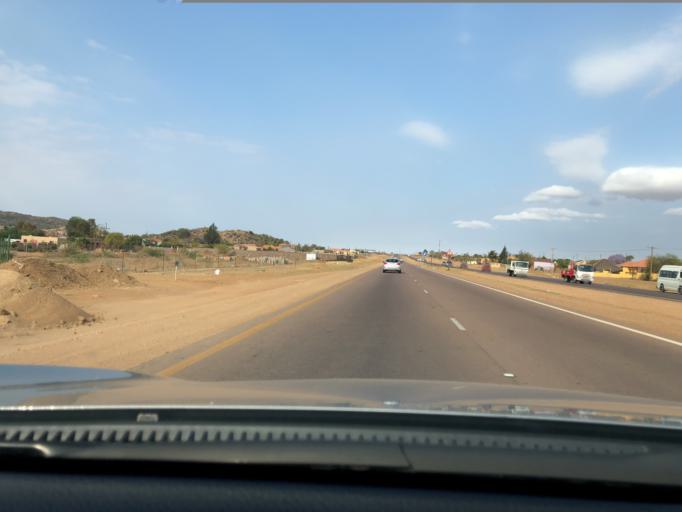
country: ZA
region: Limpopo
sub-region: Capricorn District Municipality
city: Mankoeng
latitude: -23.8918
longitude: 29.6537
